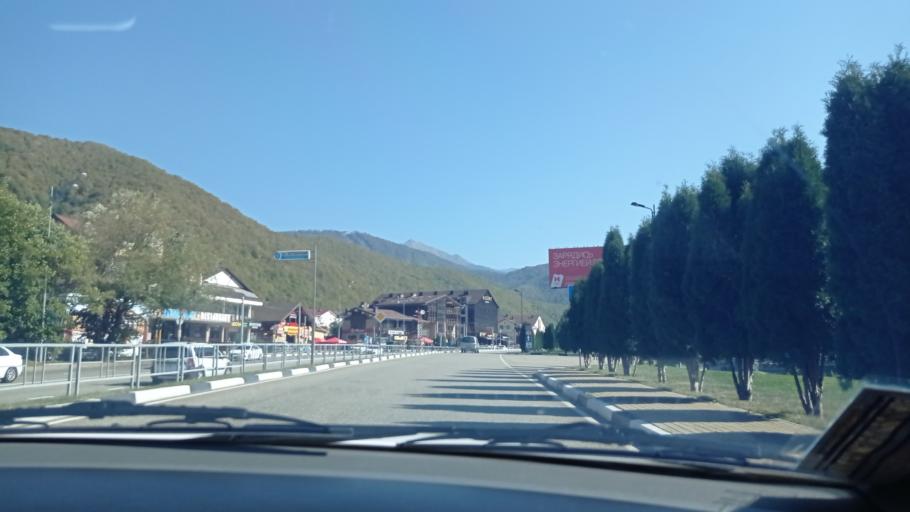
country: RU
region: Krasnodarskiy
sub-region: Sochi City
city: Krasnaya Polyana
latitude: 43.6866
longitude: 40.2491
